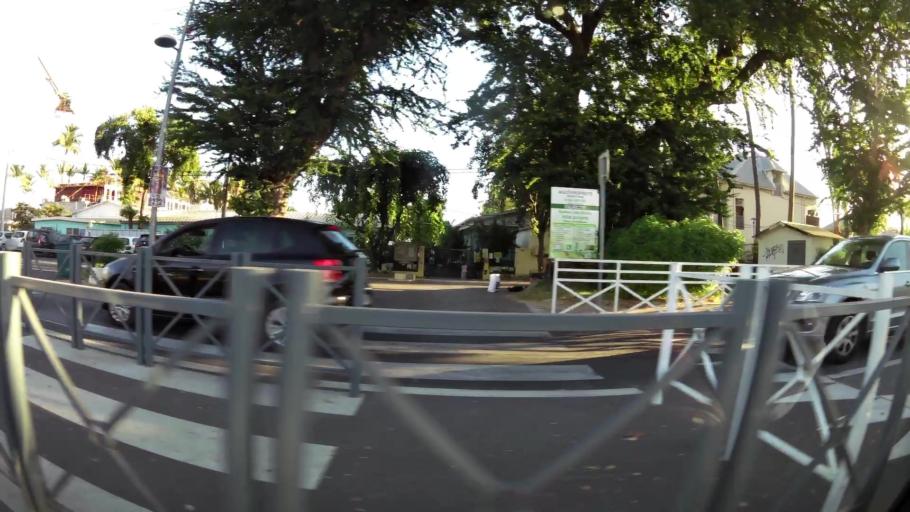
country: RE
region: Reunion
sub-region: Reunion
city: Trois-Bassins
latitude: -21.0951
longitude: 55.2373
